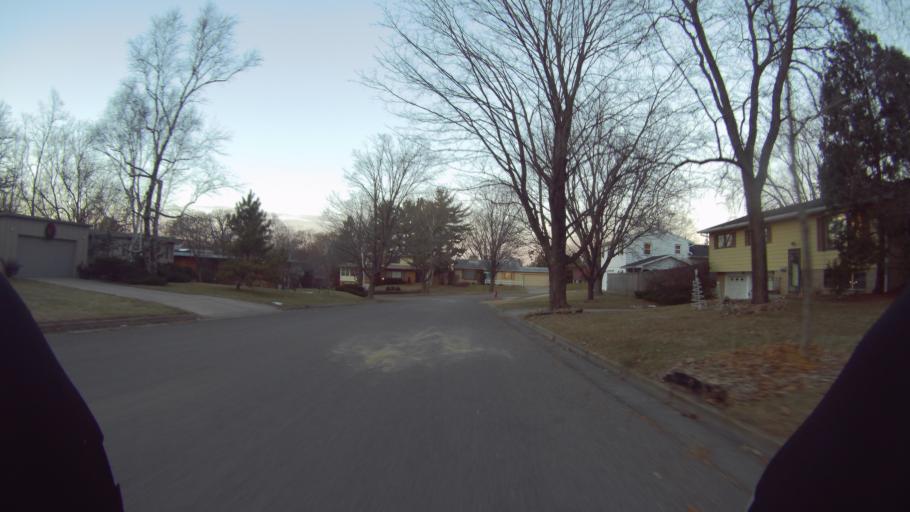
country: US
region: Wisconsin
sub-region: Dane County
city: Shorewood Hills
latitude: 43.0623
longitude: -89.4542
